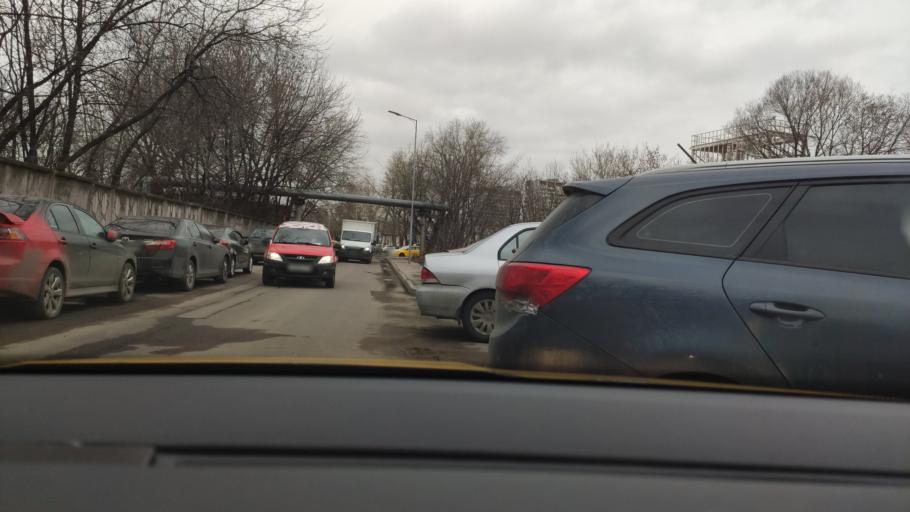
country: RU
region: Moscow
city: Lefortovo
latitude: 55.7291
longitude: 37.7134
